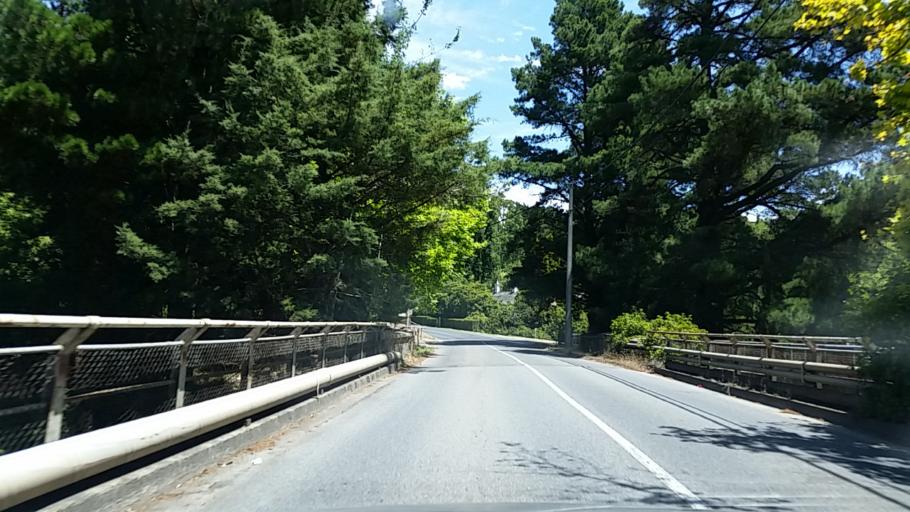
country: AU
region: South Australia
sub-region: Adelaide Hills
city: Heathfield
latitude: -35.0076
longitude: 138.7098
